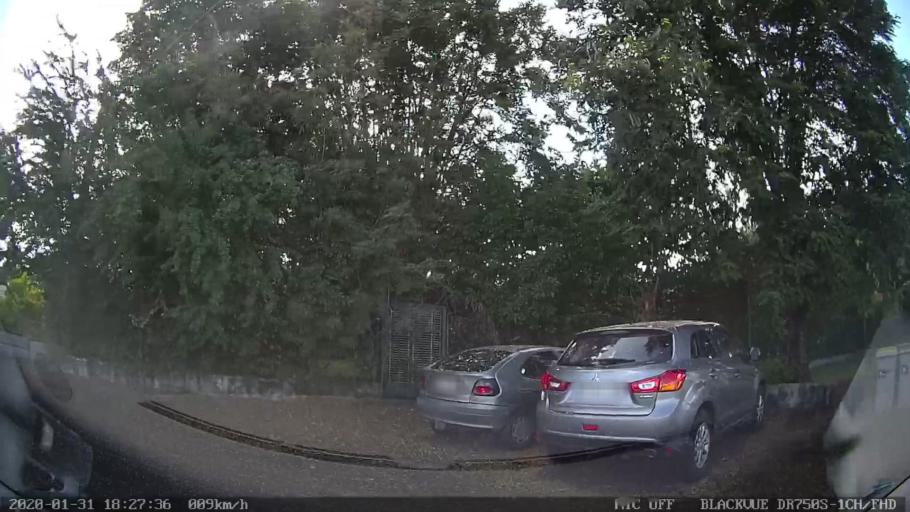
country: RE
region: Reunion
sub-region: Reunion
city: Sainte-Marie
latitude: -20.8926
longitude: 55.5090
